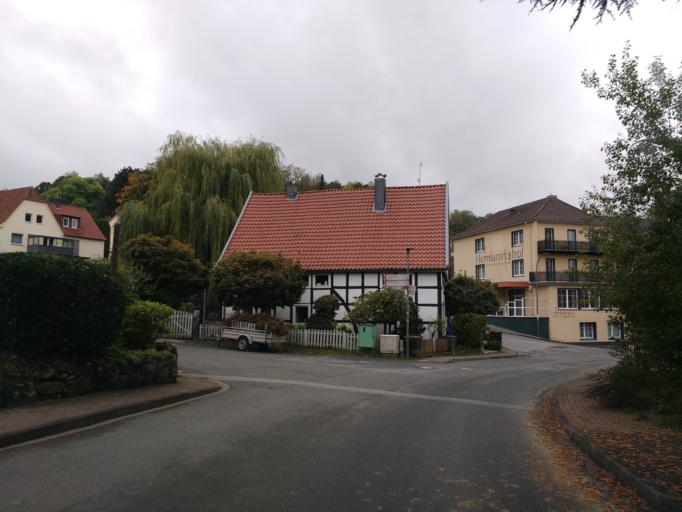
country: DE
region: North Rhine-Westphalia
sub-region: Regierungsbezirk Detmold
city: Horn
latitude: 51.8767
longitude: 8.9059
